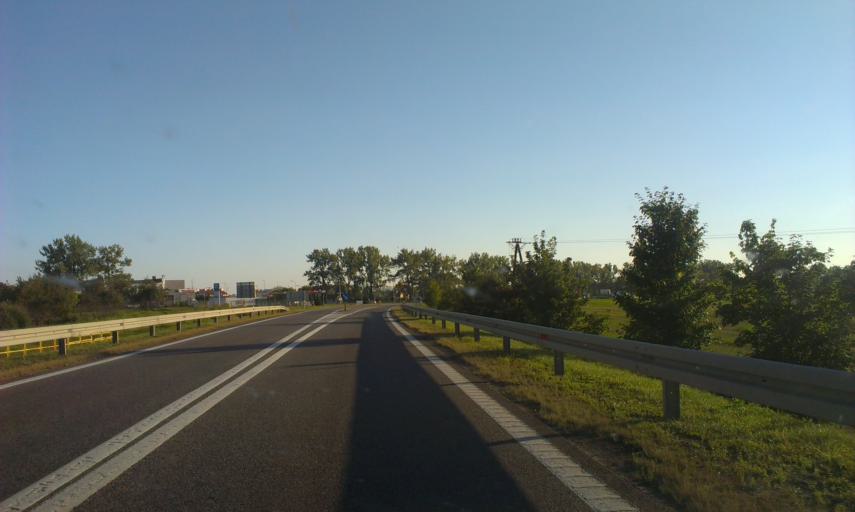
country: PL
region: Pomeranian Voivodeship
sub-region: Powiat czluchowski
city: Czluchow
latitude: 53.6610
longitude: 17.3459
